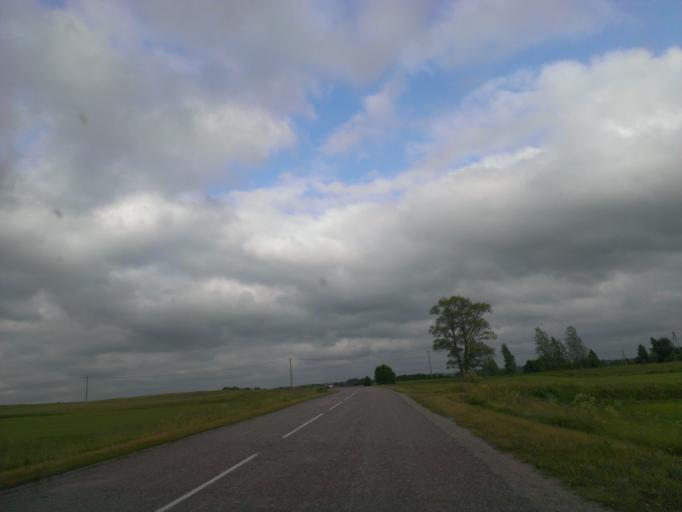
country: LV
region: Aizpute
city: Aizpute
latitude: 56.7006
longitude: 21.7819
